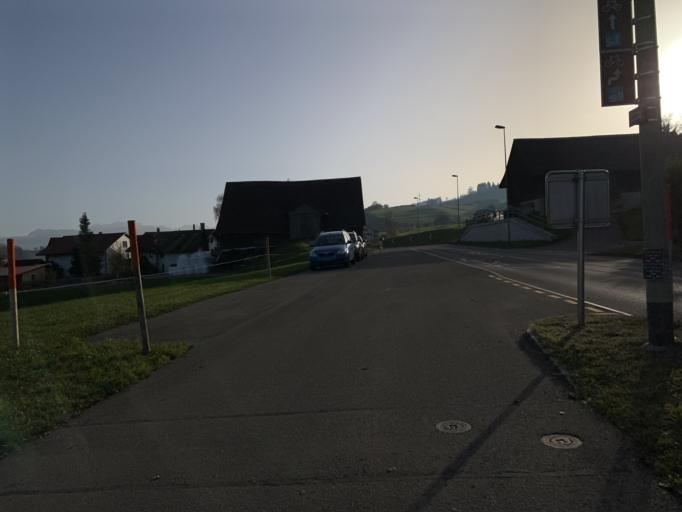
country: CH
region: Zurich
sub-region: Bezirk Hinwil
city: Wald
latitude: 47.3098
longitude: 8.9128
